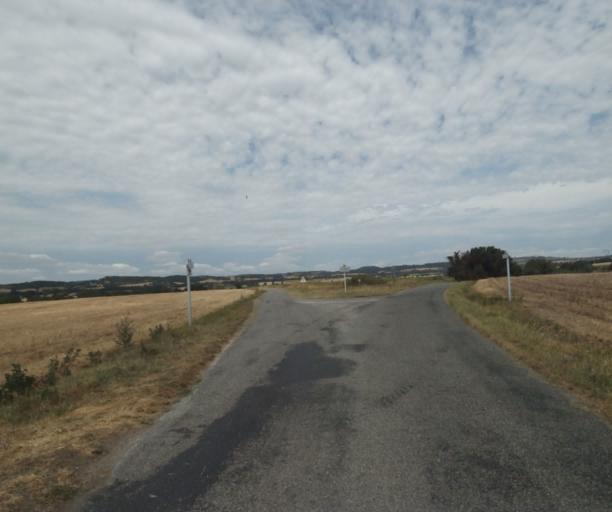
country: FR
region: Midi-Pyrenees
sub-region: Departement de la Haute-Garonne
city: Saint-Felix-Lauragais
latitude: 43.4017
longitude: 1.9068
